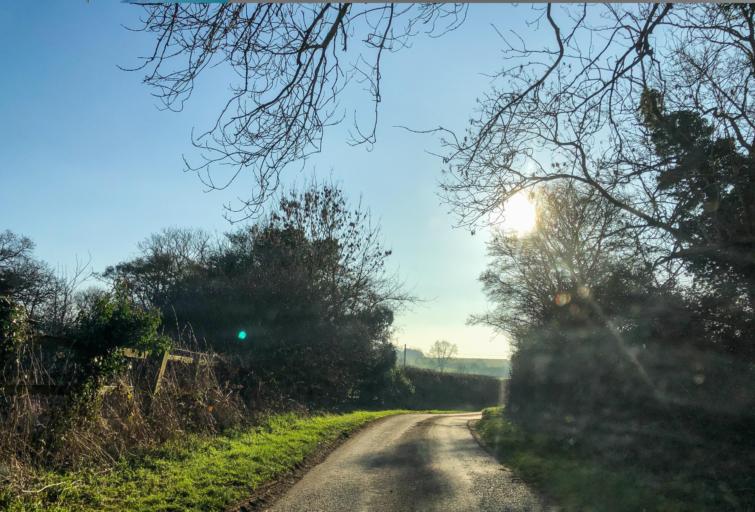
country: GB
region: England
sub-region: Warwickshire
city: Wellesbourne Mountford
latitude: 52.1997
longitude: -1.5222
